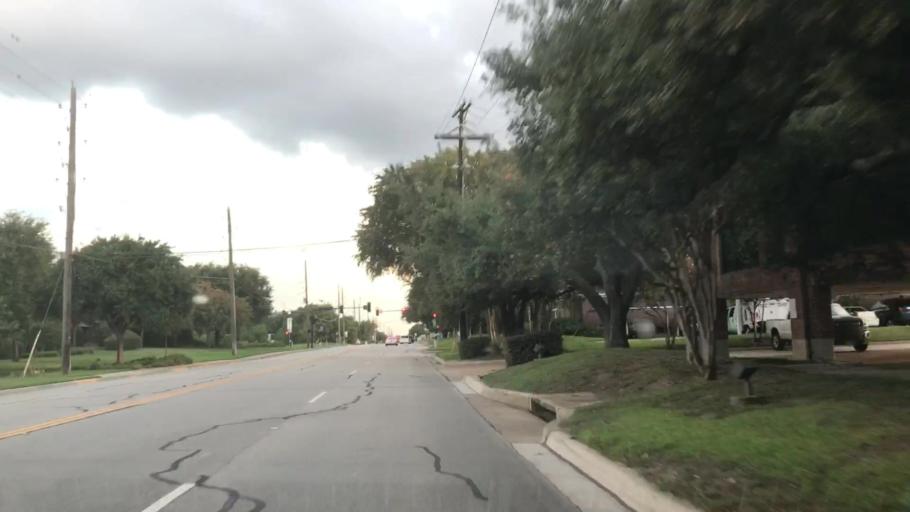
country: US
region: Texas
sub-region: Dallas County
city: Addison
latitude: 32.9674
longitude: -96.8299
